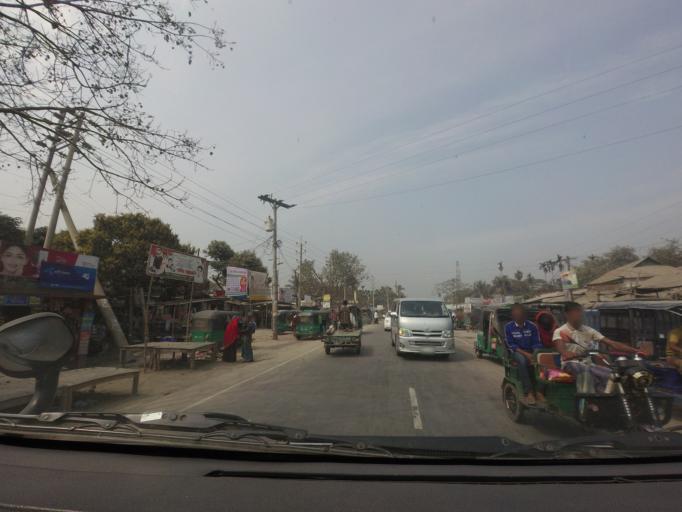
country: BD
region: Dhaka
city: Bajitpur
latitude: 24.2094
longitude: 90.8554
